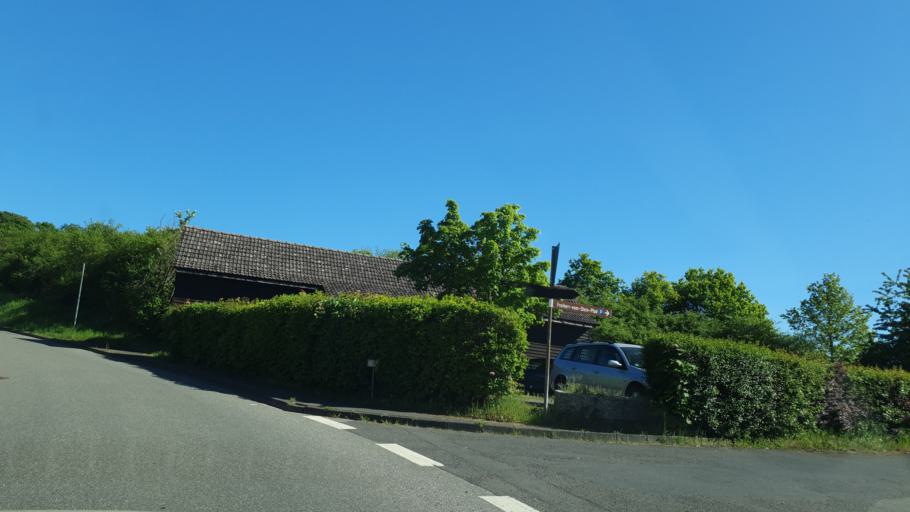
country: DE
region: Rheinland-Pfalz
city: Frucht
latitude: 50.3113
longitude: 7.6768
